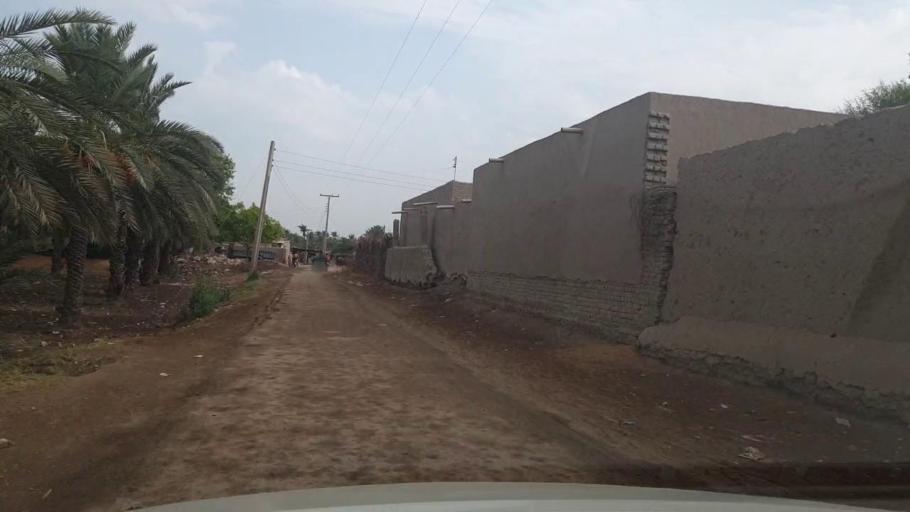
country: PK
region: Sindh
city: Khairpur
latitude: 27.6005
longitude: 68.8275
